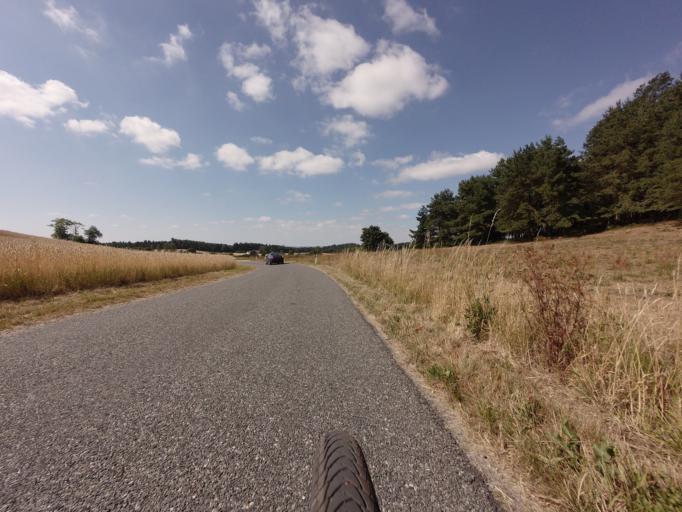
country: DK
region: Central Jutland
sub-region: Odder Kommune
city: Odder
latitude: 55.9026
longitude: 10.0626
